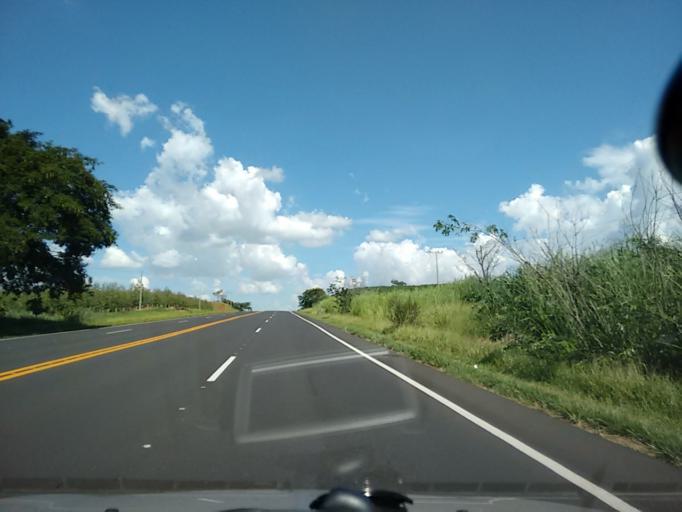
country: BR
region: Sao Paulo
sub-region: Pompeia
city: Pompeia
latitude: -22.1402
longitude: -50.1149
